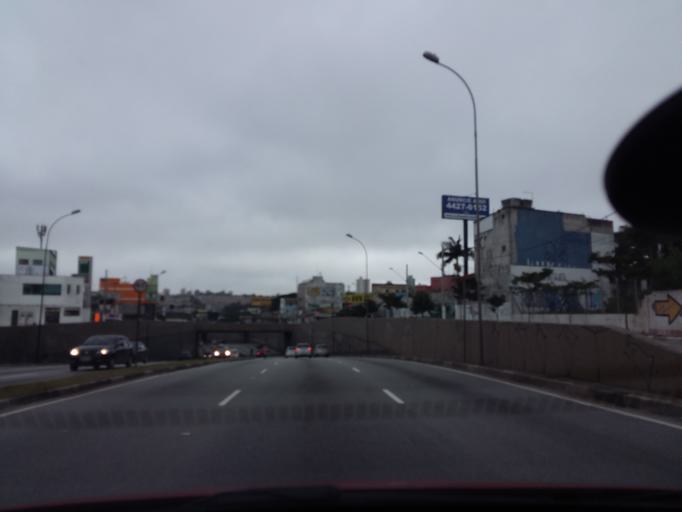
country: BR
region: Sao Paulo
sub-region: Santo Andre
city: Santo Andre
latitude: -23.6638
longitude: -46.5647
